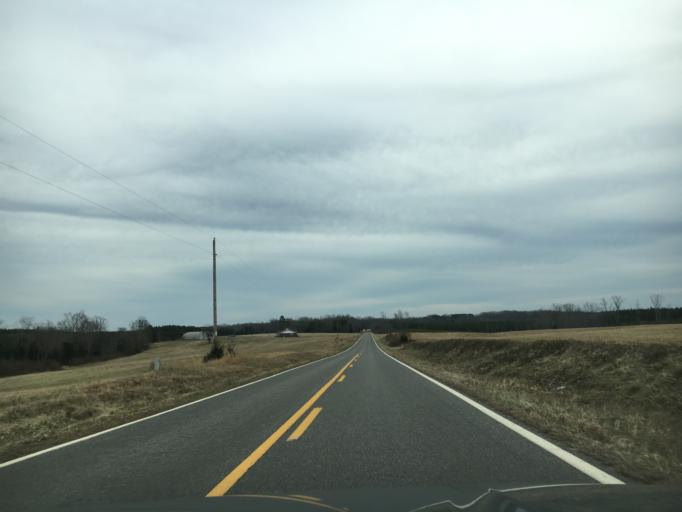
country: US
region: Virginia
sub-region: Charlotte County
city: Charlotte Court House
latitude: 37.0435
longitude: -78.7134
